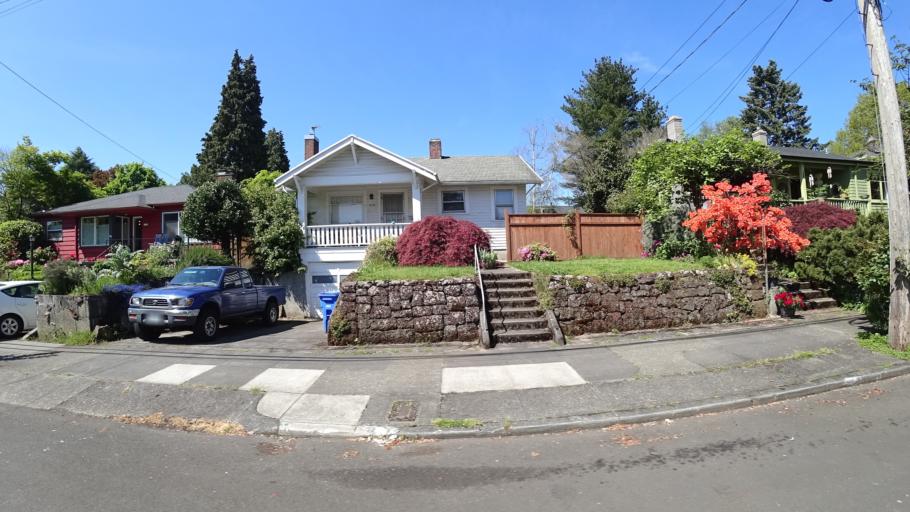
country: US
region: Oregon
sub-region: Clackamas County
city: Milwaukie
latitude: 45.4752
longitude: -122.6430
